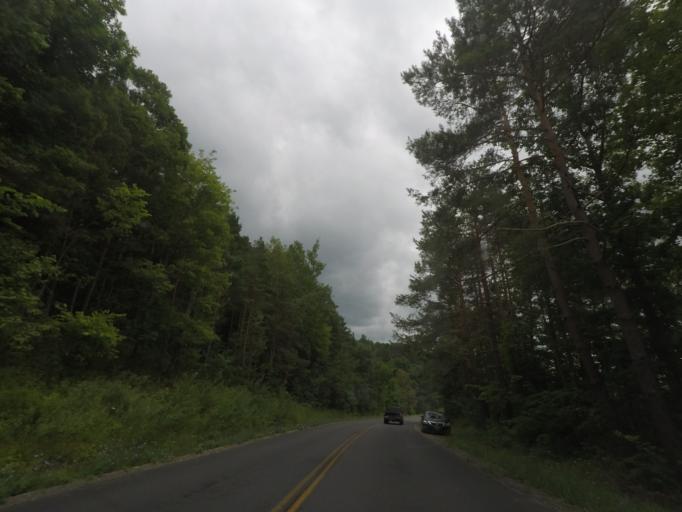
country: US
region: New York
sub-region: Rensselaer County
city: Poestenkill
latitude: 42.8281
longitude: -73.5197
